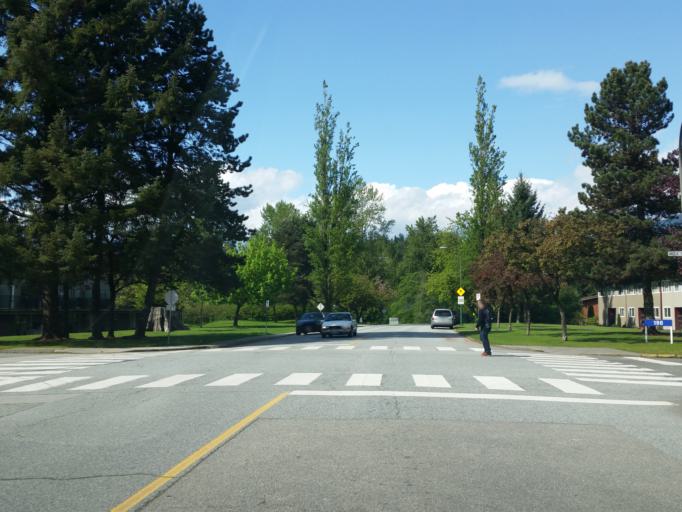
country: CA
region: British Columbia
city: Port Moody
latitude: 49.2786
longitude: -122.8755
